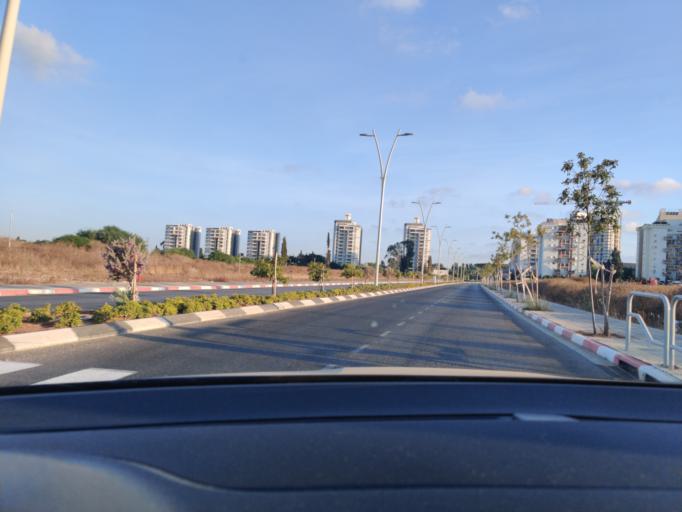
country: IL
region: Central District
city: Elyakhin
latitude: 32.4362
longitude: 34.9449
